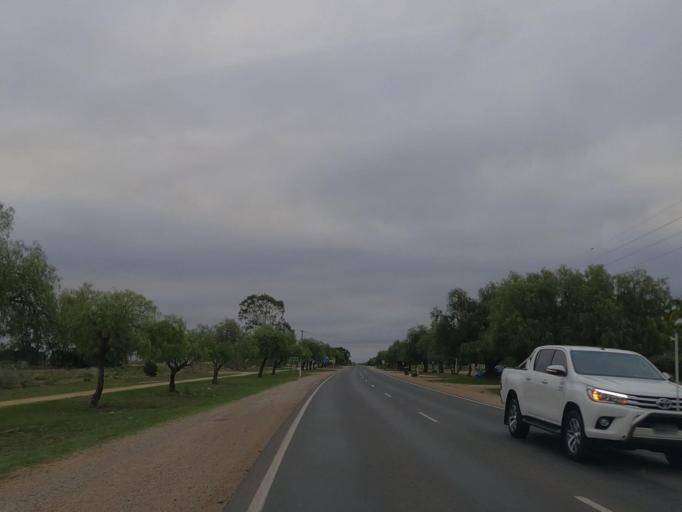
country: AU
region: Victoria
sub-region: Swan Hill
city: Swan Hill
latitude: -35.4572
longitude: 143.6302
